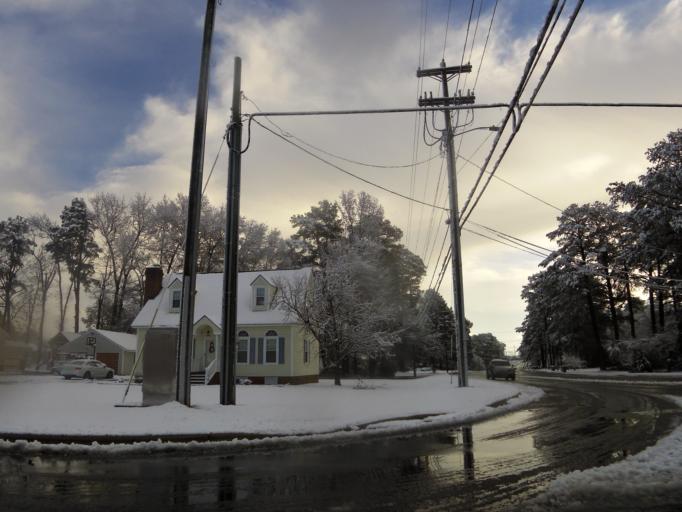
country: US
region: North Carolina
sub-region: Nash County
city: Rocky Mount
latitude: 35.9383
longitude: -77.8479
